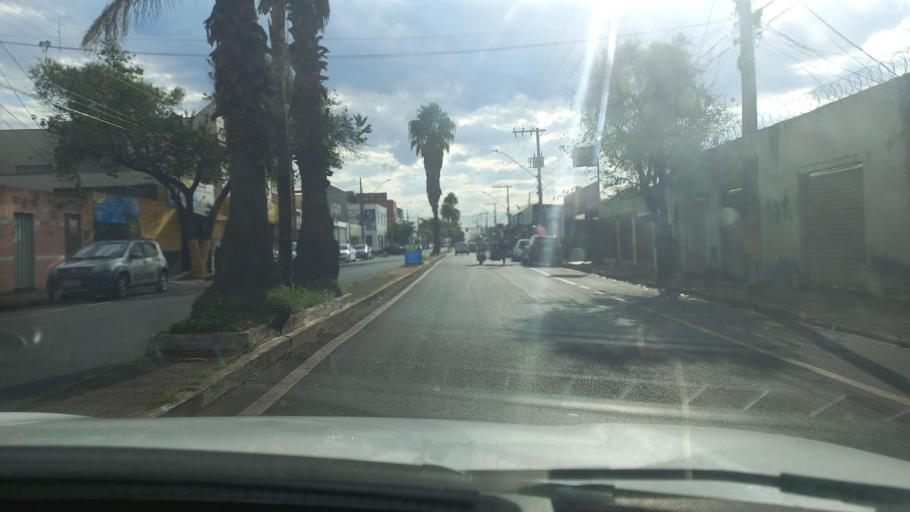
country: BR
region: Minas Gerais
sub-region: Uberaba
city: Uberaba
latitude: -19.7689
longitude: -47.9266
